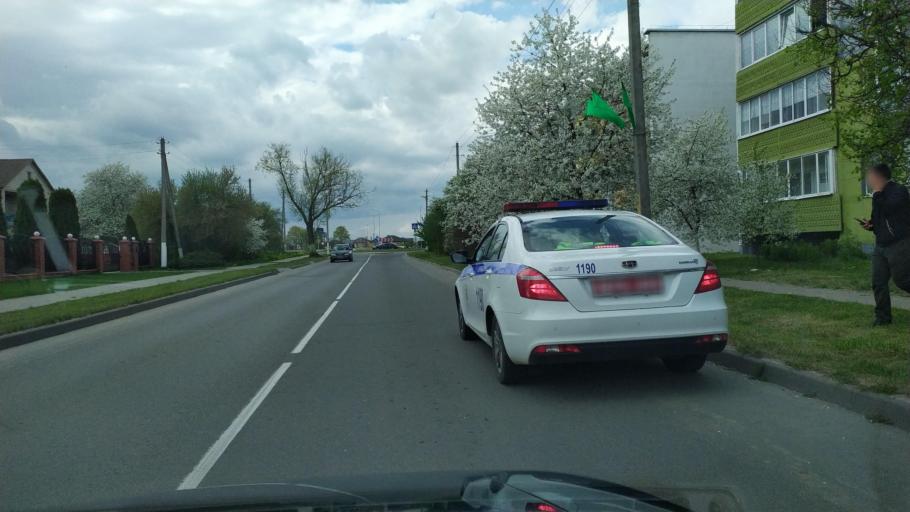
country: BY
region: Brest
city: Pruzhany
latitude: 52.5584
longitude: 24.4293
